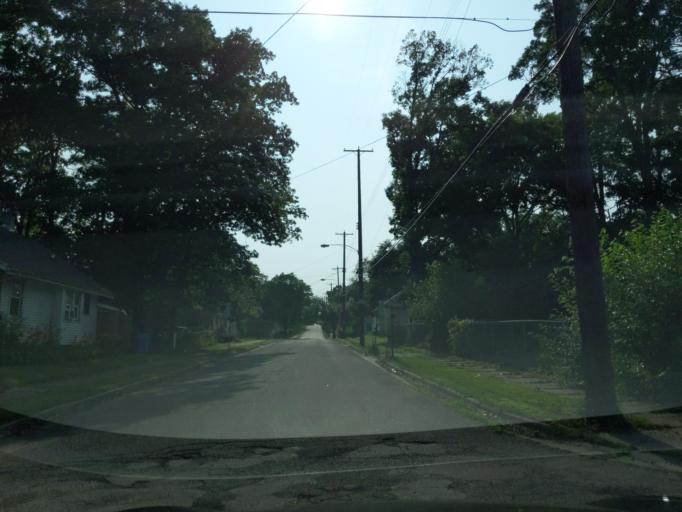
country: US
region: Michigan
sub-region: Ingham County
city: Lansing
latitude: 42.7211
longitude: -84.5250
